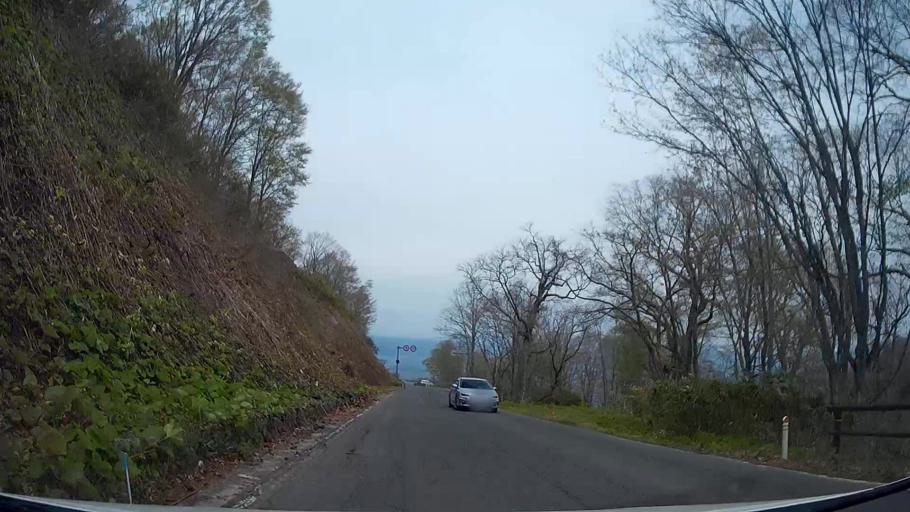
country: JP
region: Akita
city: Hanawa
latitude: 40.4070
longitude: 140.8651
